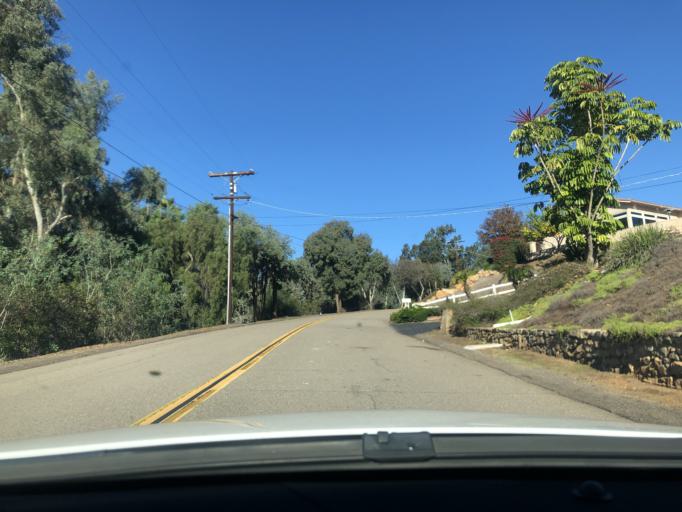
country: US
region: California
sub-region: San Diego County
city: Casa de Oro-Mount Helix
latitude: 32.7647
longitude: -116.9553
